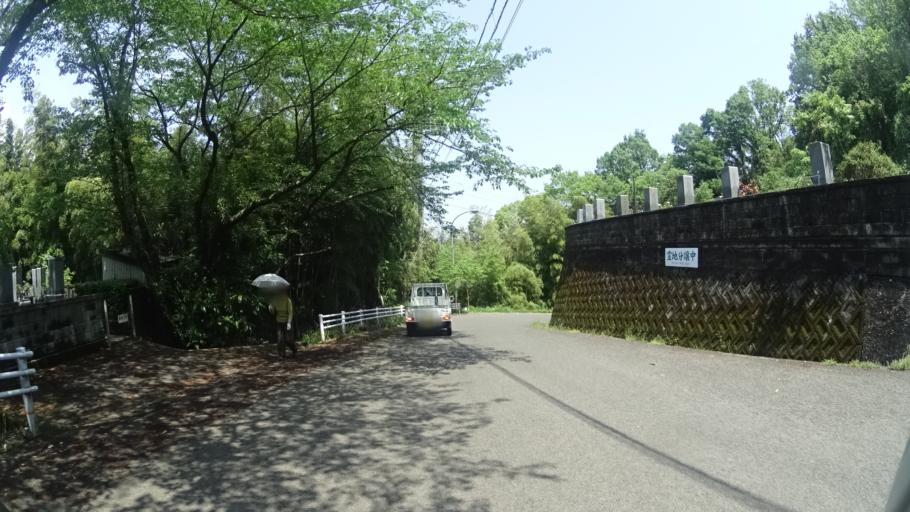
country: JP
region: Tokushima
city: Tokushima-shi
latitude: 34.0696
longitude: 134.5130
